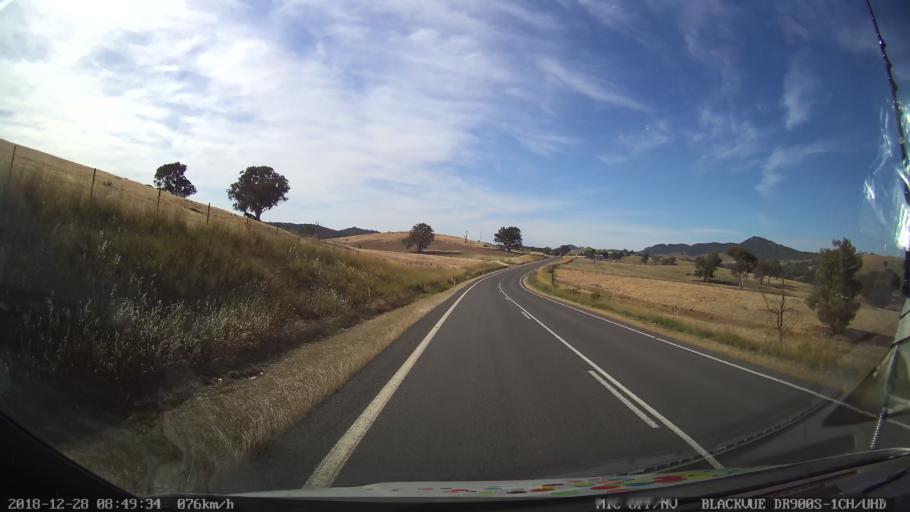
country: AU
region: New South Wales
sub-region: Upper Lachlan Shire
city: Crookwell
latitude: -34.0469
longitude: 149.3374
